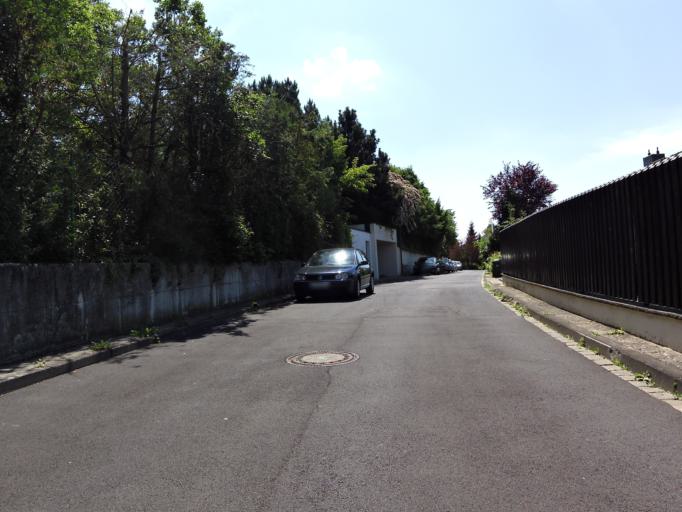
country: DE
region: Bavaria
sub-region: Regierungsbezirk Unterfranken
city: Wuerzburg
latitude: 49.7763
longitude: 9.9473
